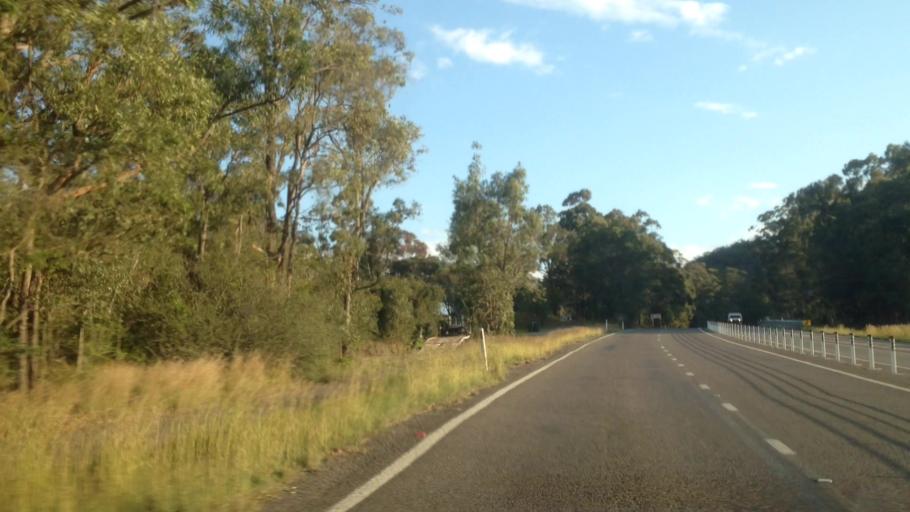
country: AU
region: New South Wales
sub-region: Lake Macquarie Shire
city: Cooranbong
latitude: -32.9576
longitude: 151.4809
